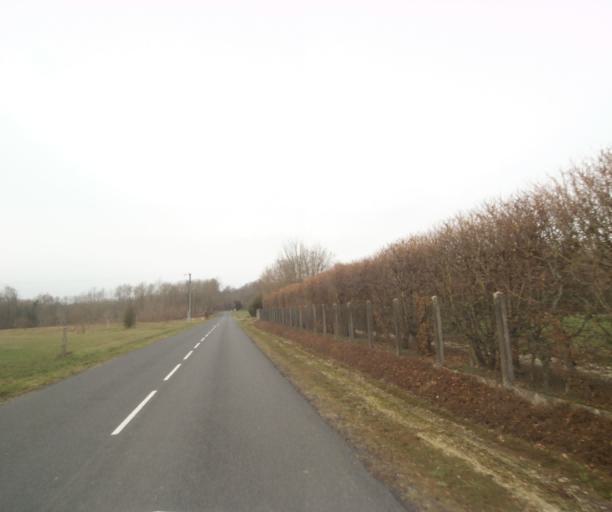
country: FR
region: Champagne-Ardenne
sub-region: Departement de la Marne
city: Sermaize-les-Bains
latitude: 48.7361
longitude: 4.8944
